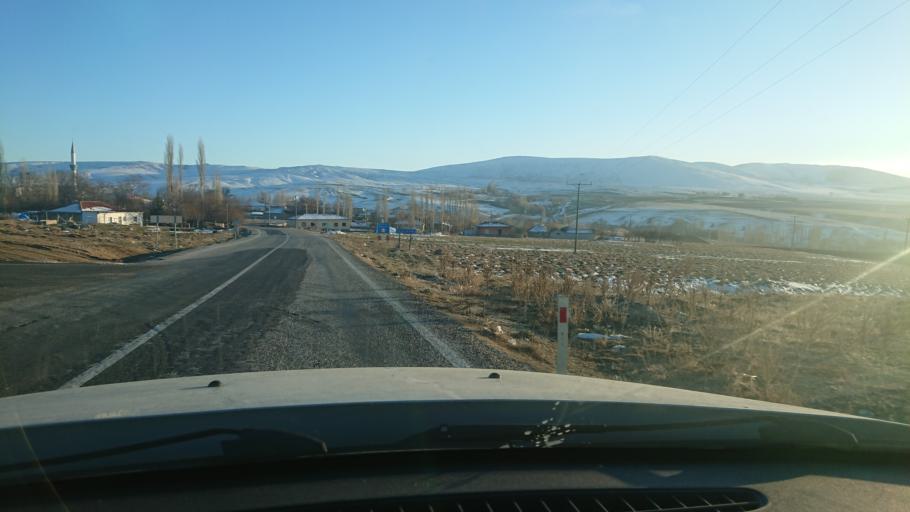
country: TR
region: Aksaray
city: Ortakoy
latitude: 38.7587
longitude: 33.9336
